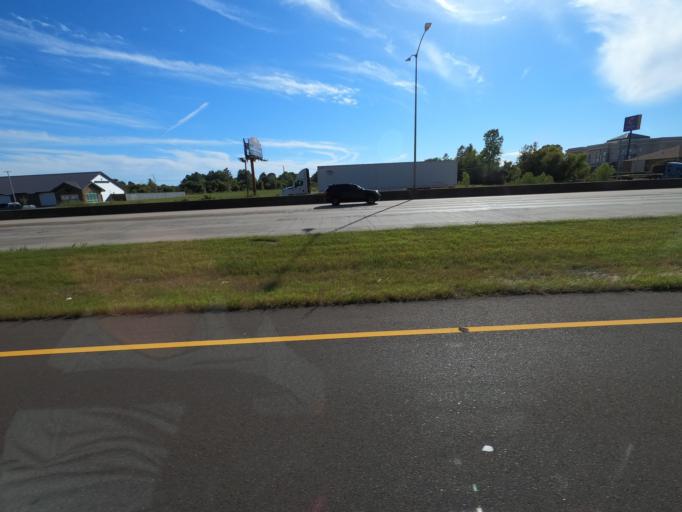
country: US
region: Arkansas
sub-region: Crittenden County
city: West Memphis
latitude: 35.1632
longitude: -90.1701
